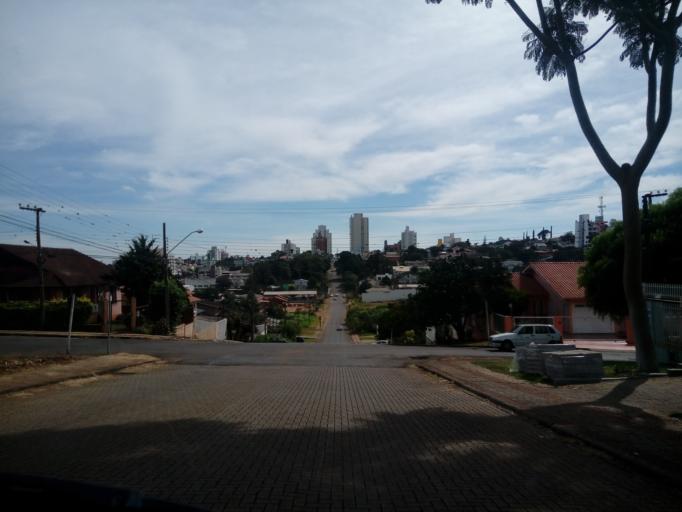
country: BR
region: Santa Catarina
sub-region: Chapeco
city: Chapeco
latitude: -27.1189
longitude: -52.6140
